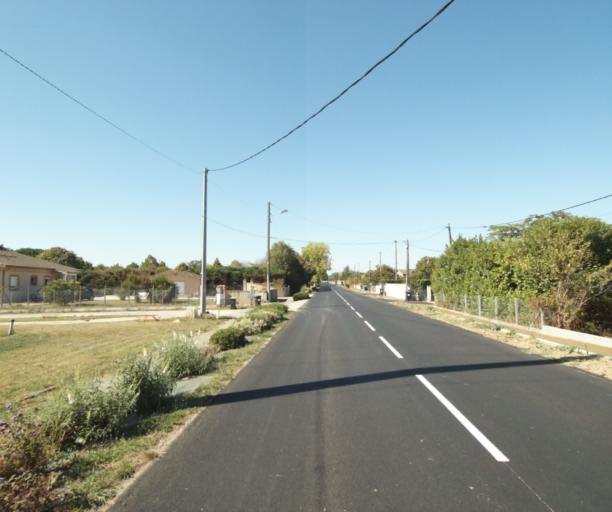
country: FR
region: Midi-Pyrenees
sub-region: Departement du Tarn-et-Garonne
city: Verdun-sur-Garonne
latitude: 43.8486
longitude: 1.2211
